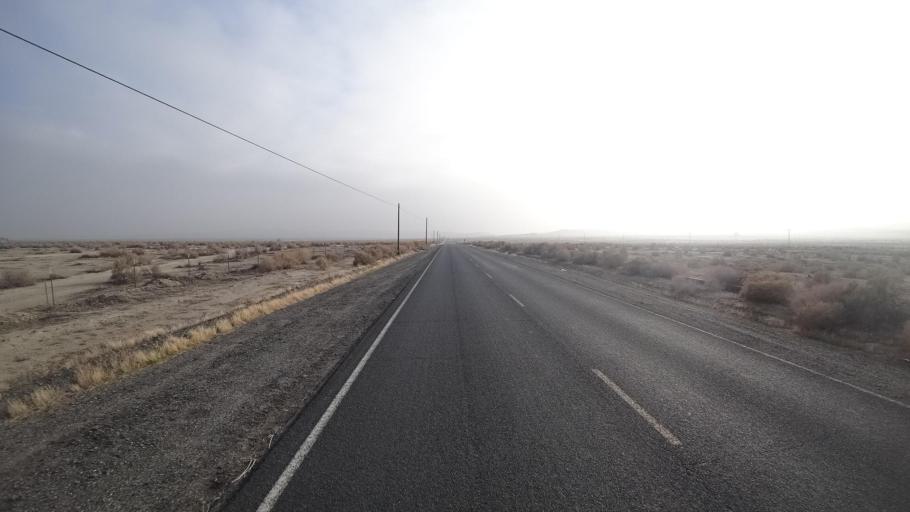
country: US
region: California
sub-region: Kern County
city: Ford City
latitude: 35.2183
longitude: -119.4456
